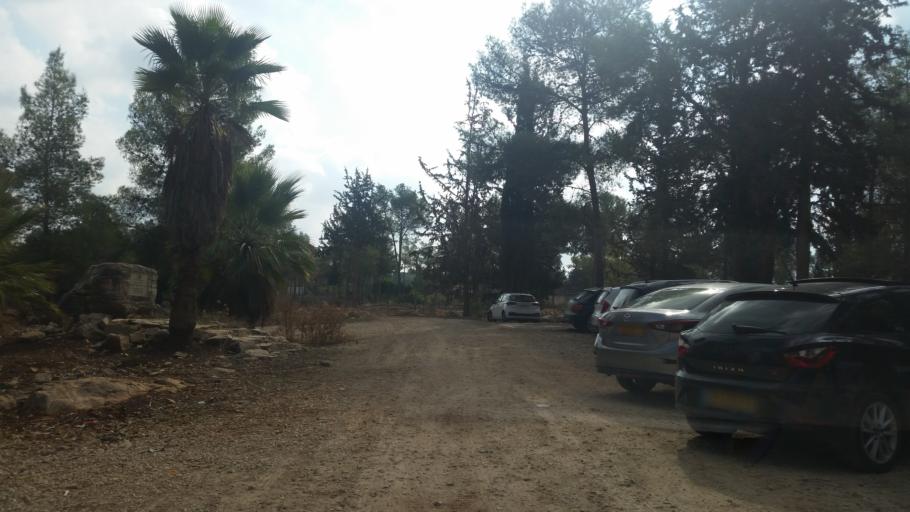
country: IL
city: Hashmonaim
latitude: 31.9233
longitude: 35.0117
